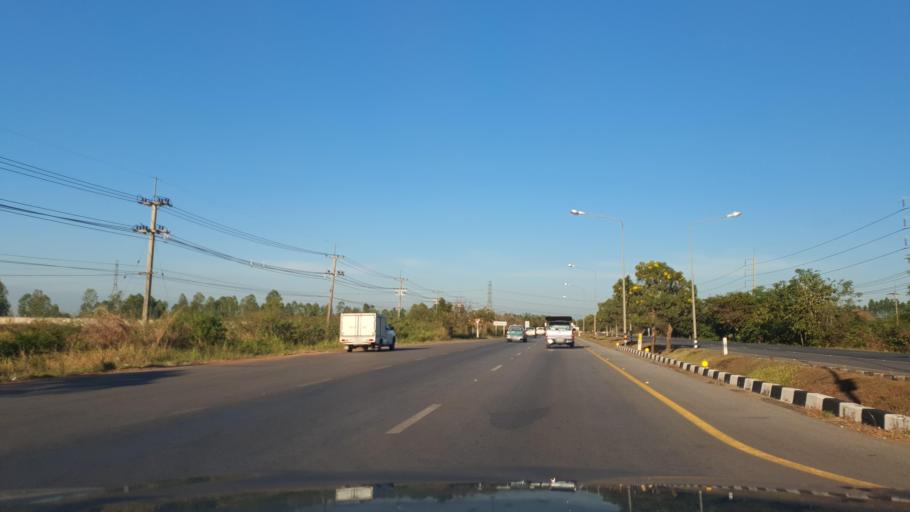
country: TH
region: Phitsanulok
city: Phitsanulok
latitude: 16.8523
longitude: 100.3295
